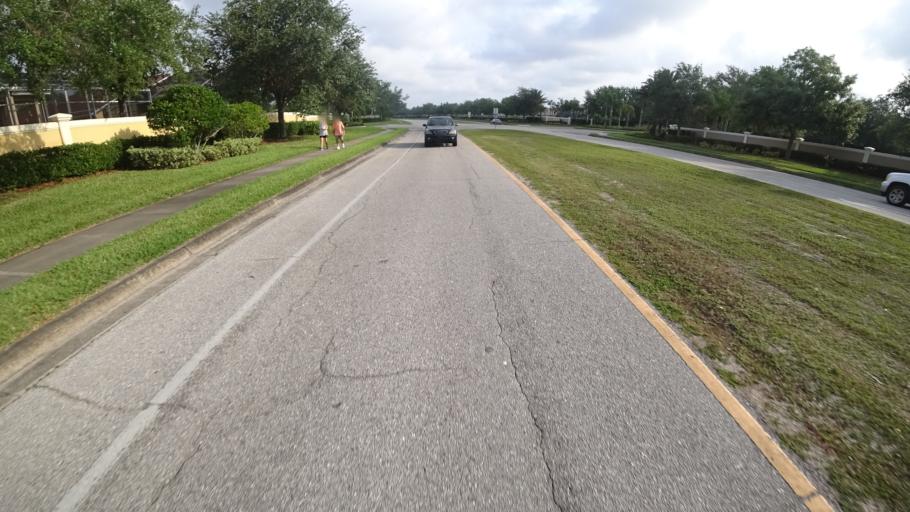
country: US
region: Florida
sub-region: Sarasota County
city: North Sarasota
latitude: 27.4225
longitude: -82.5128
